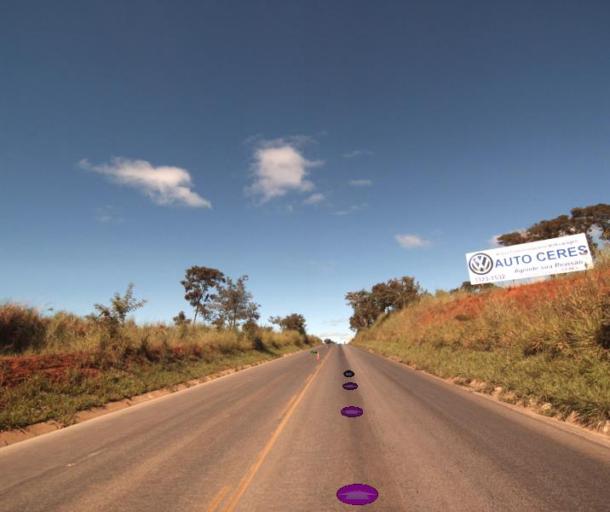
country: BR
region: Goias
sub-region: Itapaci
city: Itapaci
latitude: -15.0967
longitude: -49.4748
